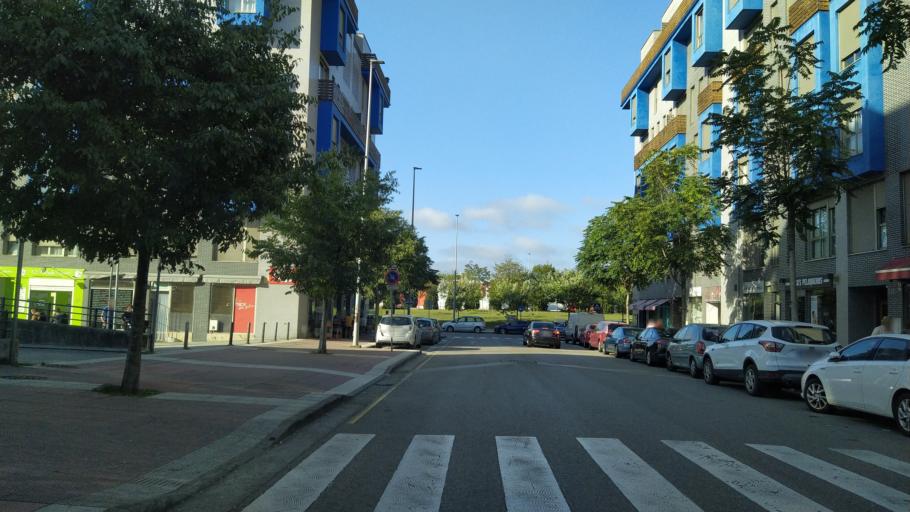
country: ES
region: Cantabria
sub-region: Provincia de Cantabria
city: El Astillero
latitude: 43.4387
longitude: -3.8412
